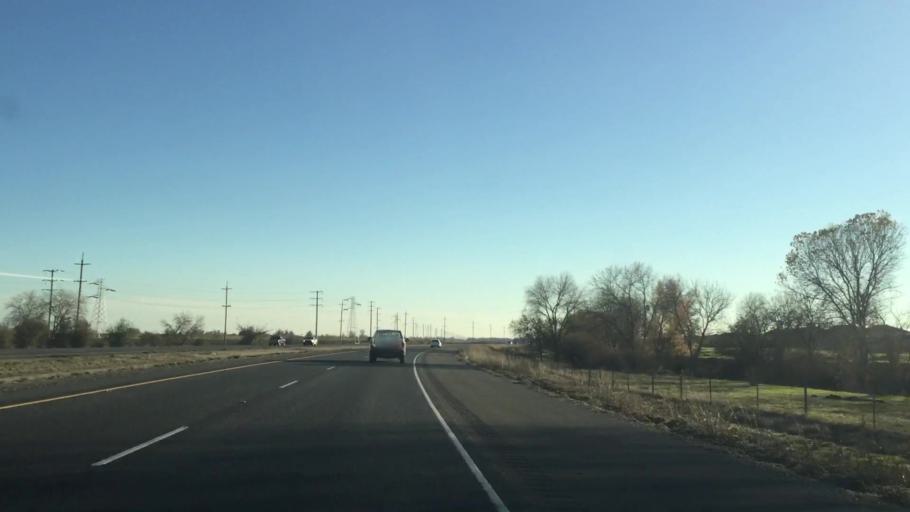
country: US
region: California
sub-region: Yuba County
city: Plumas Lake
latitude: 39.0144
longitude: -121.5440
